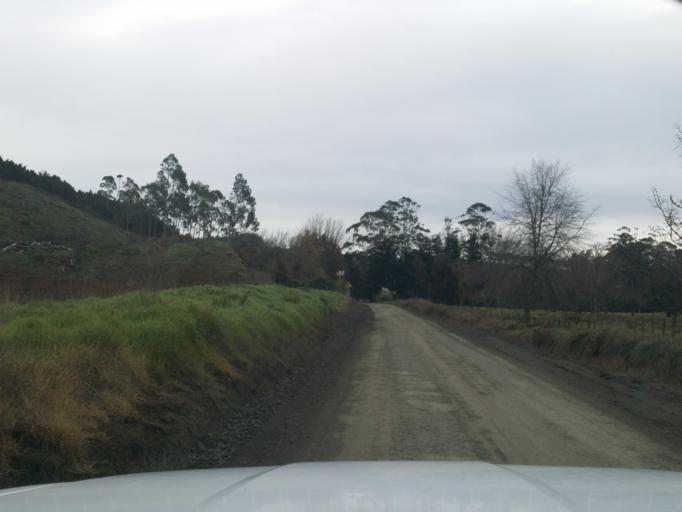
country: NZ
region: Northland
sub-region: Whangarei
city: Maungatapere
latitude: -35.8148
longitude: 174.0364
